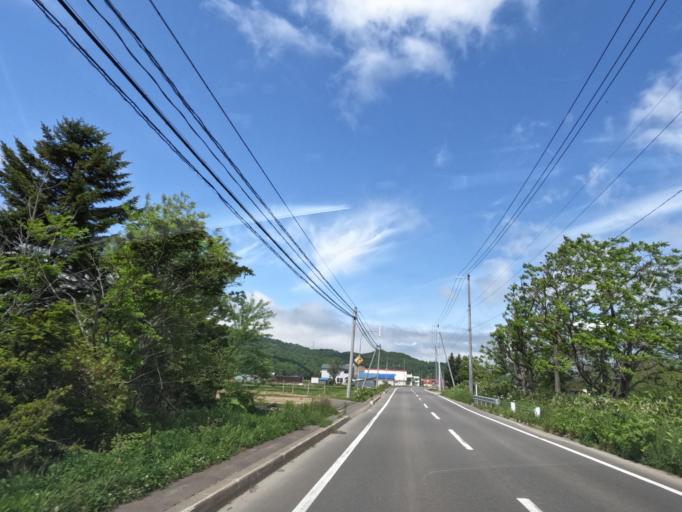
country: JP
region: Hokkaido
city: Tobetsu
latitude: 43.2831
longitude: 141.5364
